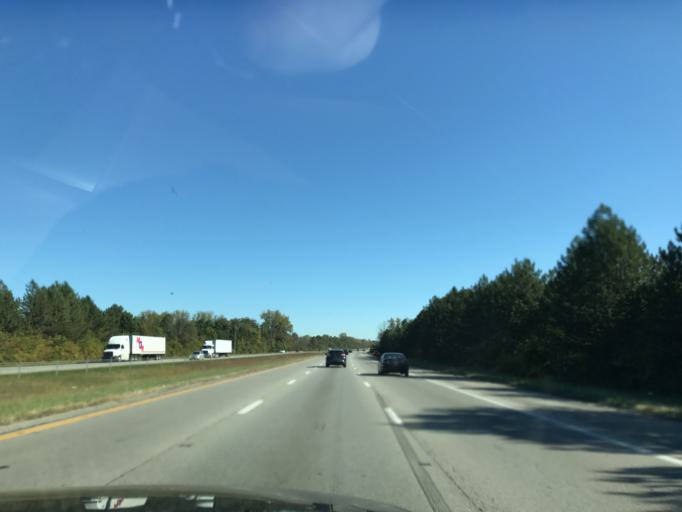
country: US
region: Ohio
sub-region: Franklin County
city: Blacklick Estates
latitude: 39.9185
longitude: -82.8787
